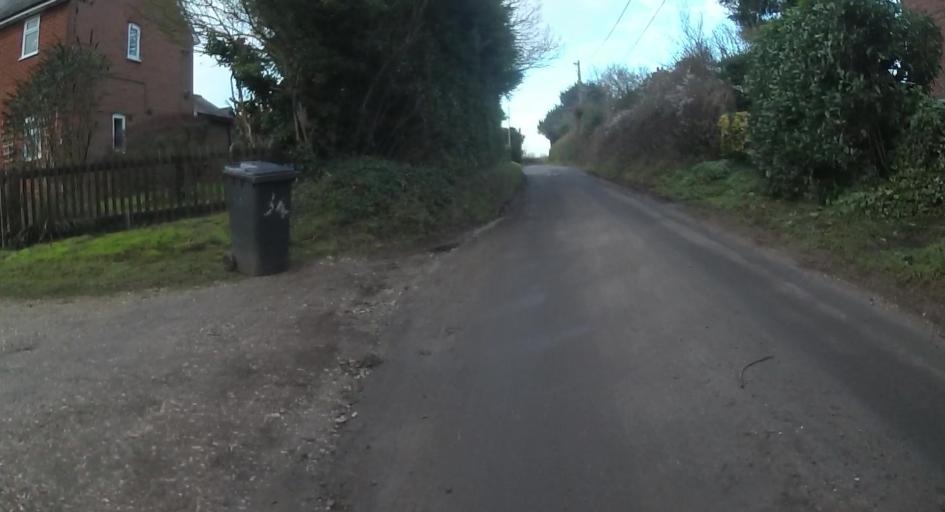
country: GB
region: England
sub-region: Hampshire
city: Basingstoke
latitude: 51.2765
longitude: -1.1528
